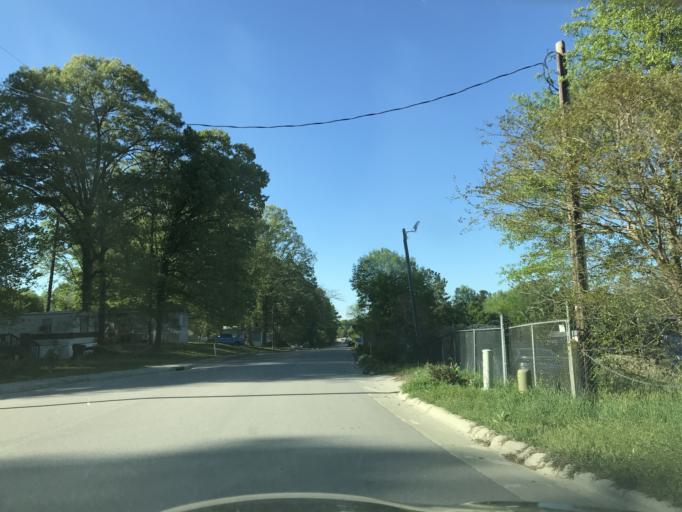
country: US
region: North Carolina
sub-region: Wake County
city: Knightdale
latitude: 35.7921
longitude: -78.5566
